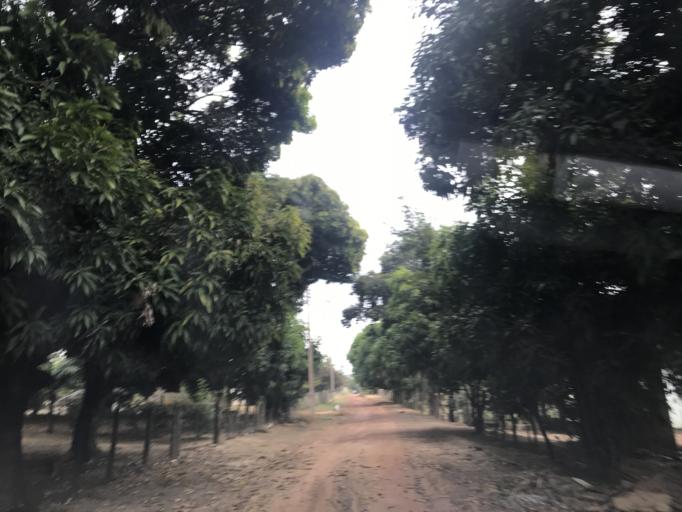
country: BR
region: Goias
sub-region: Padre Bernardo
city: Padre Bernardo
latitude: -15.3581
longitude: -48.2324
